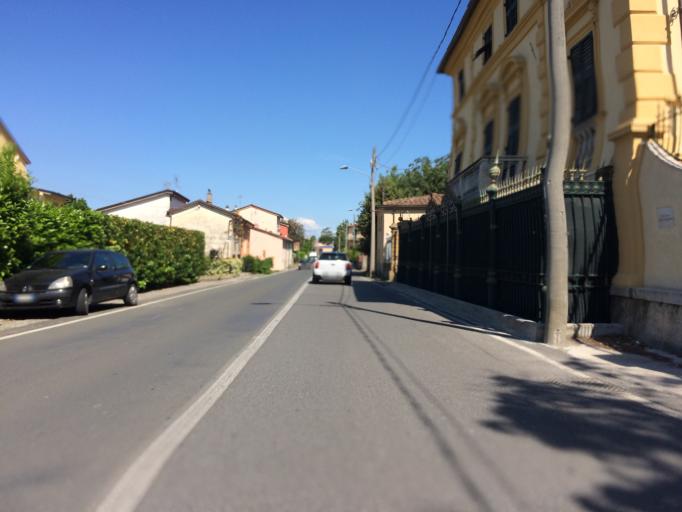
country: IT
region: Liguria
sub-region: Provincia di La Spezia
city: Sarzana
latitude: 44.1048
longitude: 9.9756
